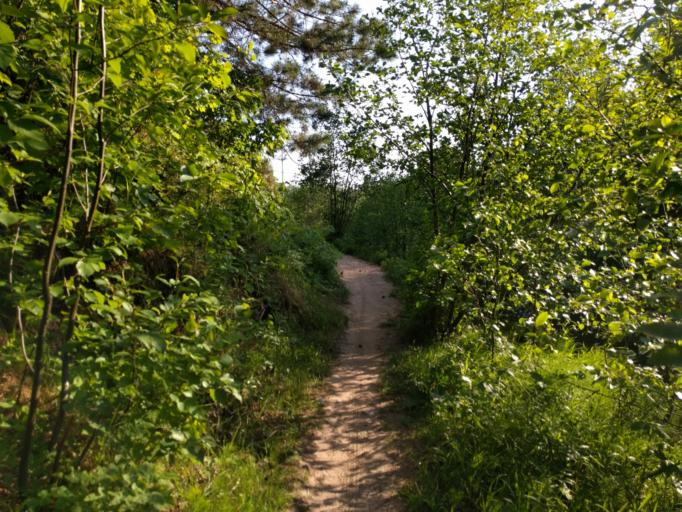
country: US
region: Michigan
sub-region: Marquette County
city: Trowbridge Park
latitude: 46.5680
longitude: -87.4458
